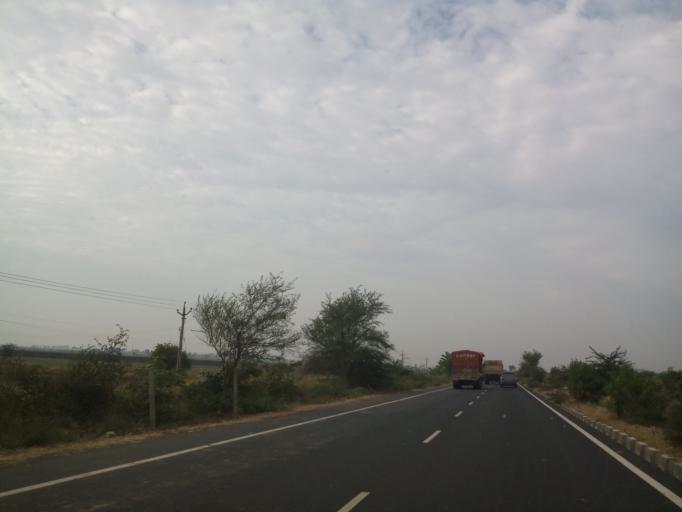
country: IN
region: Gujarat
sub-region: Ahmadabad
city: Dholka
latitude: 22.7328
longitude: 72.2811
